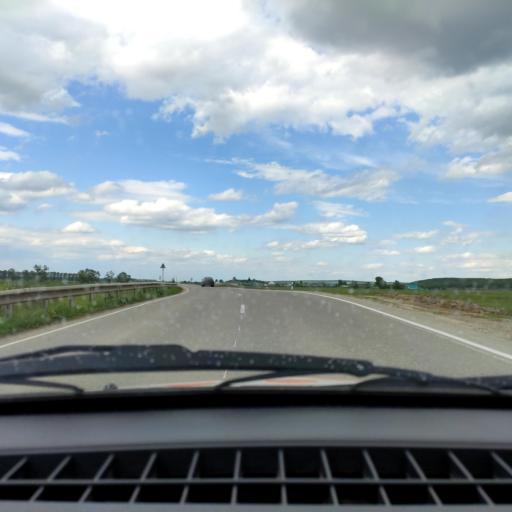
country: RU
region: Bashkortostan
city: Iglino
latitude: 54.9404
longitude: 56.4793
